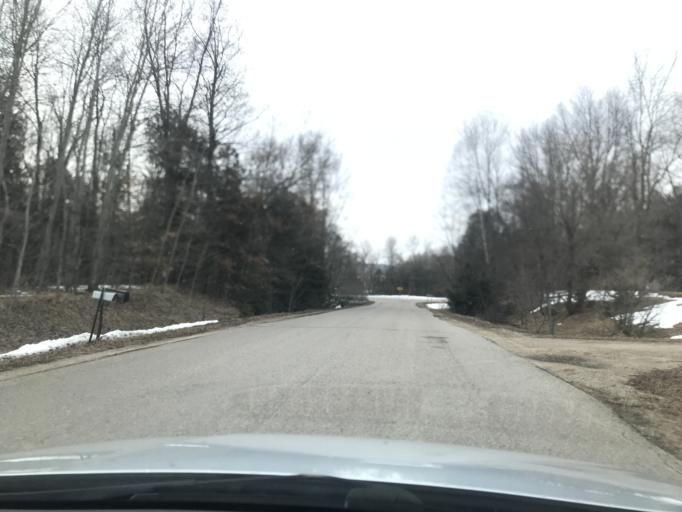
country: US
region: Wisconsin
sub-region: Oconto County
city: Oconto Falls
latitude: 44.8516
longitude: -88.1472
